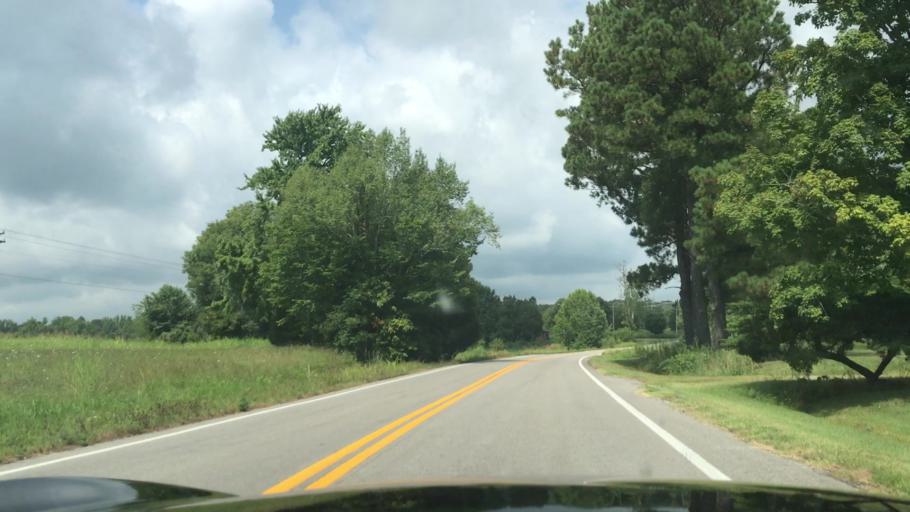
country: US
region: Kentucky
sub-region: Muhlenberg County
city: Central City
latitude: 37.1953
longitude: -86.9907
